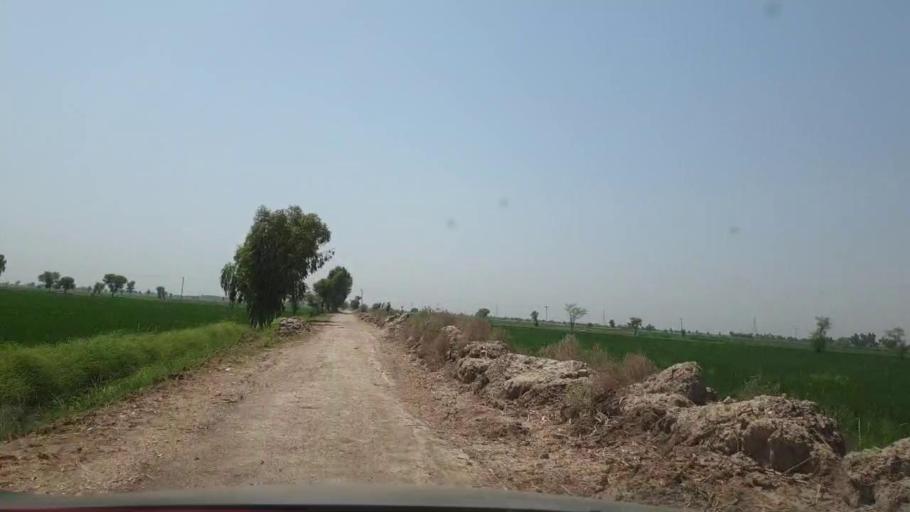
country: PK
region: Sindh
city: Warah
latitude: 27.5076
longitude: 67.7658
